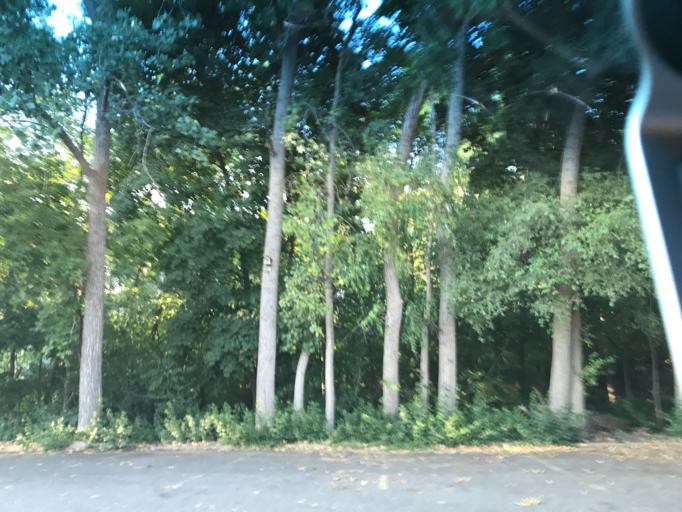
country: US
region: Michigan
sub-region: Washtenaw County
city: Ypsilanti
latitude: 42.2511
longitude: -83.6620
